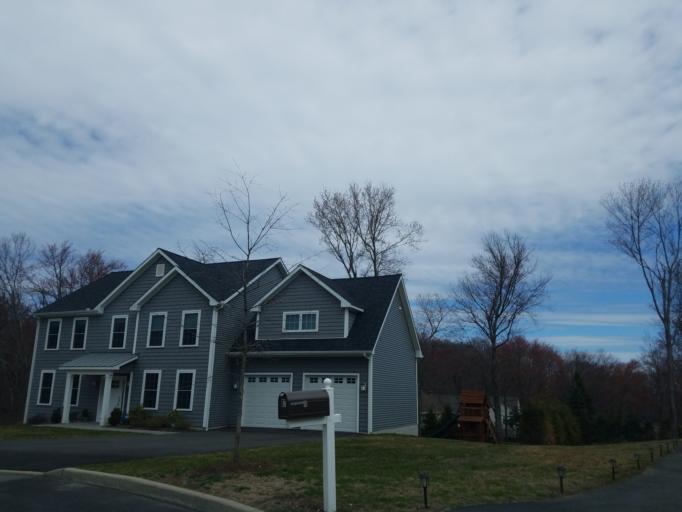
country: US
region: Connecticut
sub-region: Fairfield County
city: Bridgeport
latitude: 41.1917
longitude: -73.2416
